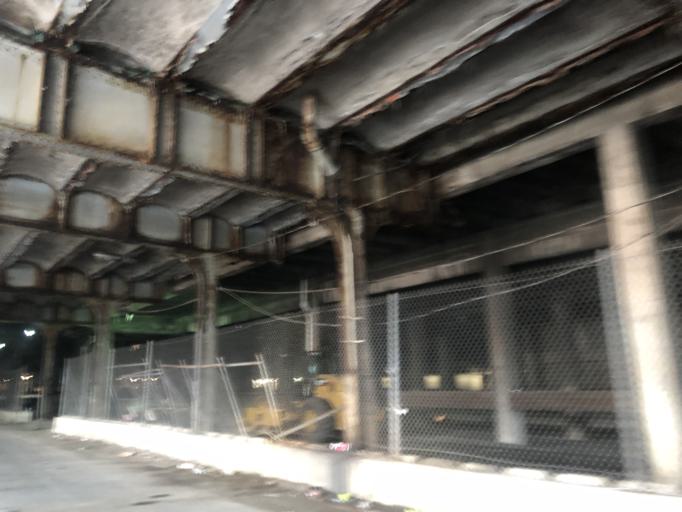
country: US
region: Pennsylvania
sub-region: Philadelphia County
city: Philadelphia
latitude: 39.9540
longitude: -75.1836
